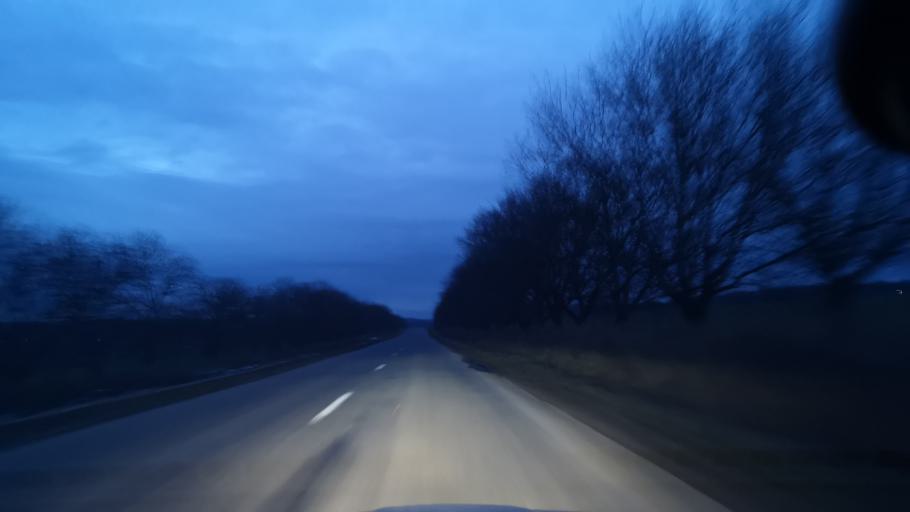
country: MD
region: Orhei
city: Orhei
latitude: 47.2887
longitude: 28.8186
